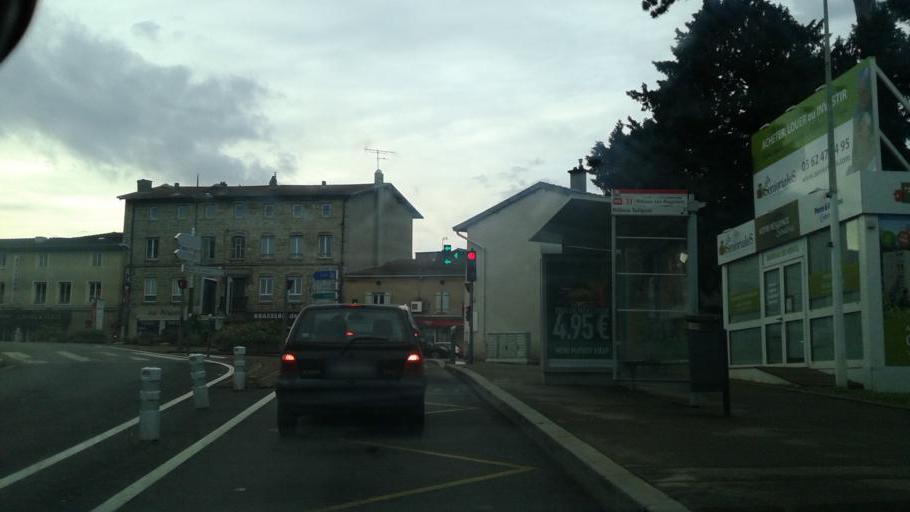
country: FR
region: Rhone-Alpes
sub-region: Departement du Rhone
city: Rillieux-la-Pape
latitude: 45.8211
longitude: 4.8963
